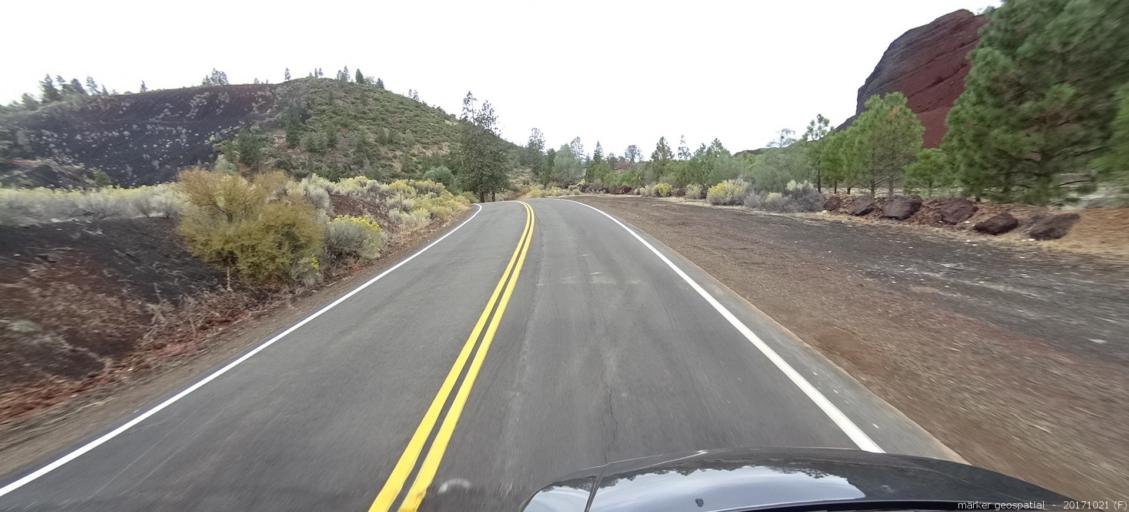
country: US
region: California
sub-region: Shasta County
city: Burney
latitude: 40.9252
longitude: -121.4641
